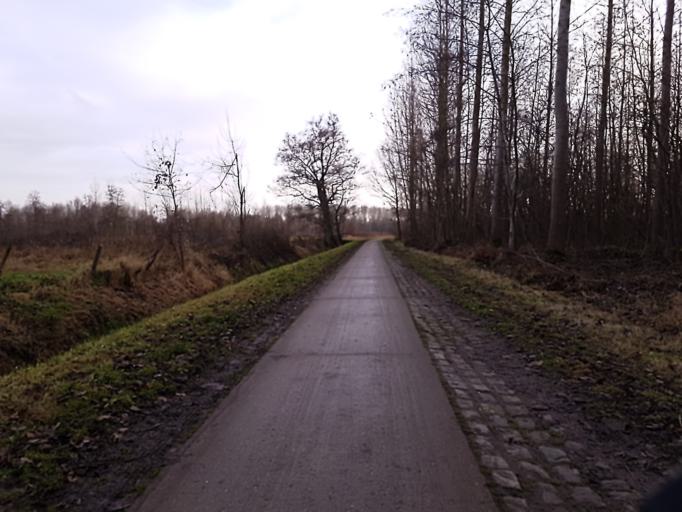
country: BE
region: Flanders
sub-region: Provincie Vlaams-Brabant
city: Rotselaar
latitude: 50.9418
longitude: 4.7024
